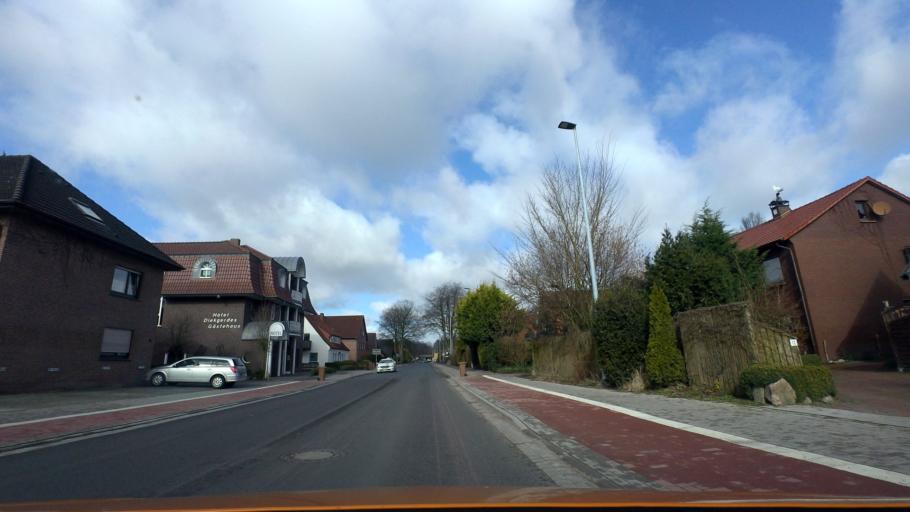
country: DE
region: Lower Saxony
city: Cloppenburg
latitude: 52.8520
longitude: 8.0366
